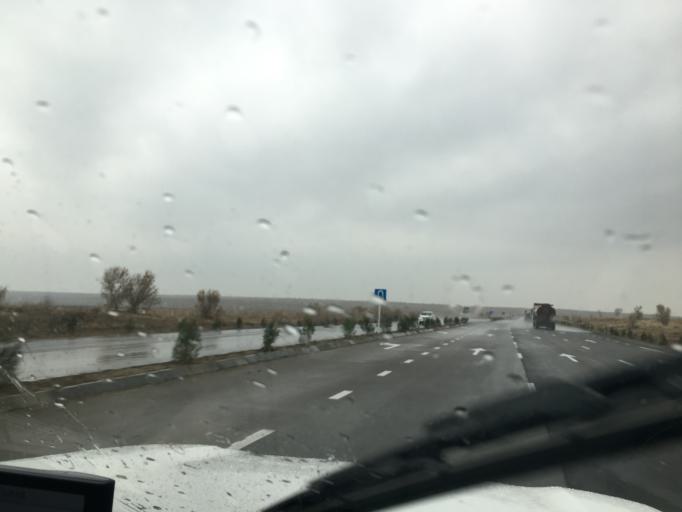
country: TM
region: Ahal
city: Annau
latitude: 37.8730
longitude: 58.6508
